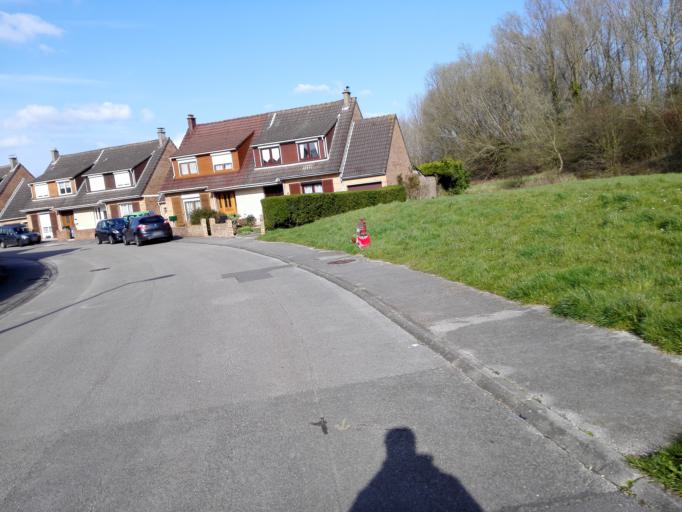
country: FR
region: Nord-Pas-de-Calais
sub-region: Departement du Nord
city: Grande-Synthe
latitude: 51.0014
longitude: 2.2925
